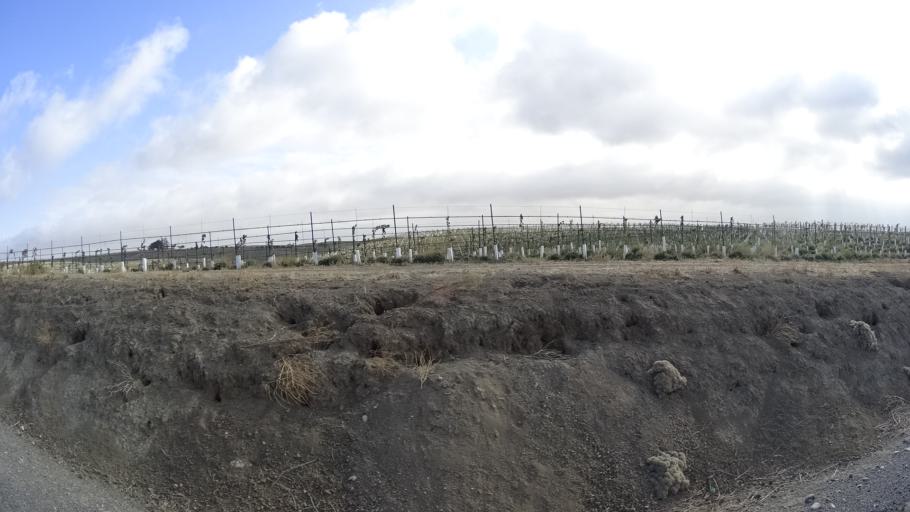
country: US
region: California
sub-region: Yolo County
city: Dunnigan
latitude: 38.7956
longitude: -122.0074
